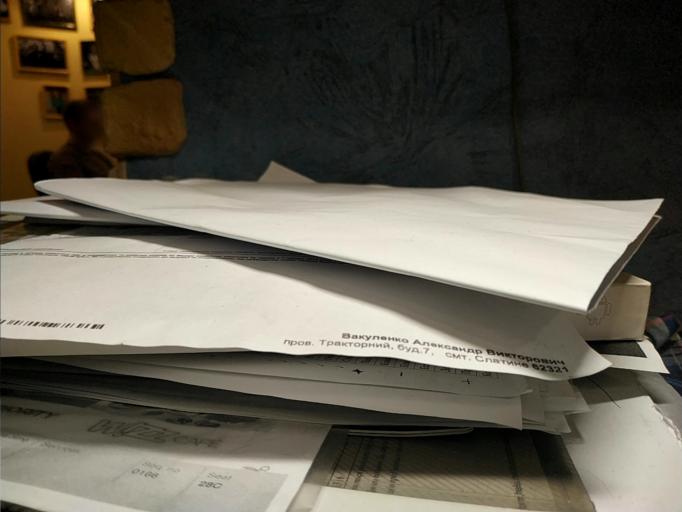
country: RU
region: Tverskaya
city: Zubtsov
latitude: 56.1062
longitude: 34.6534
